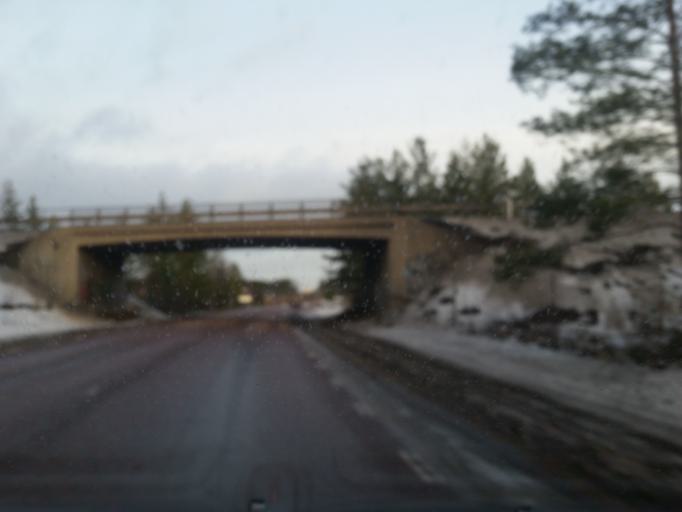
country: SE
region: Gaevleborg
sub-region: Sandvikens Kommun
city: Sandviken
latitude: 60.6272
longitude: 16.7528
